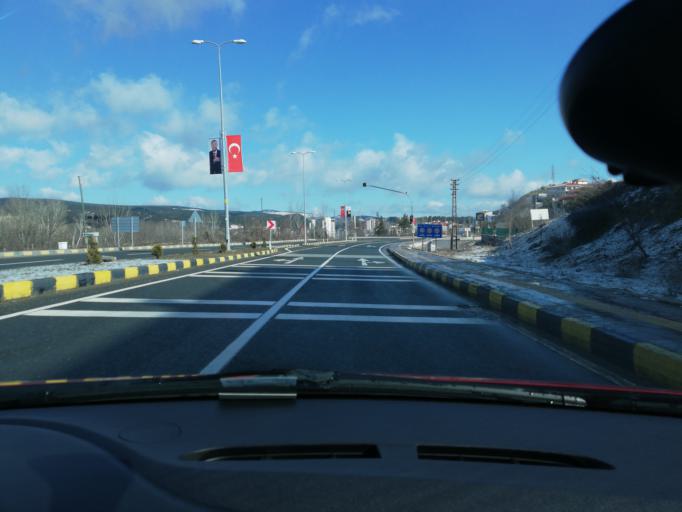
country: TR
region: Kastamonu
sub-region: Cide
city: Kastamonu
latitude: 41.3488
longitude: 33.7658
